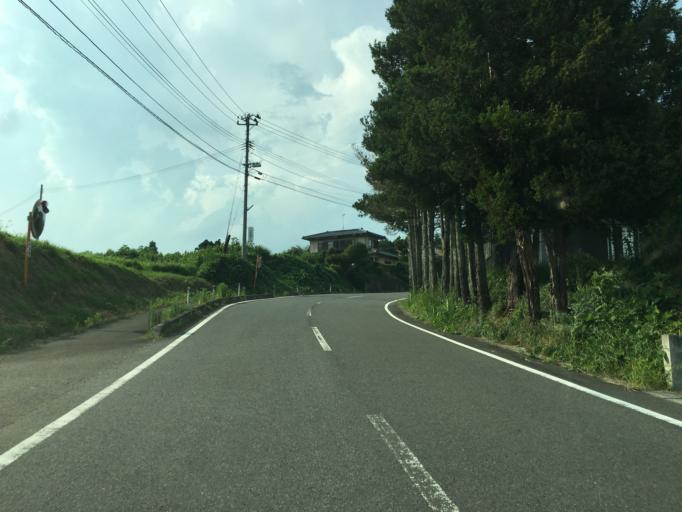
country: JP
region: Fukushima
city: Miharu
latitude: 37.4272
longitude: 140.4532
